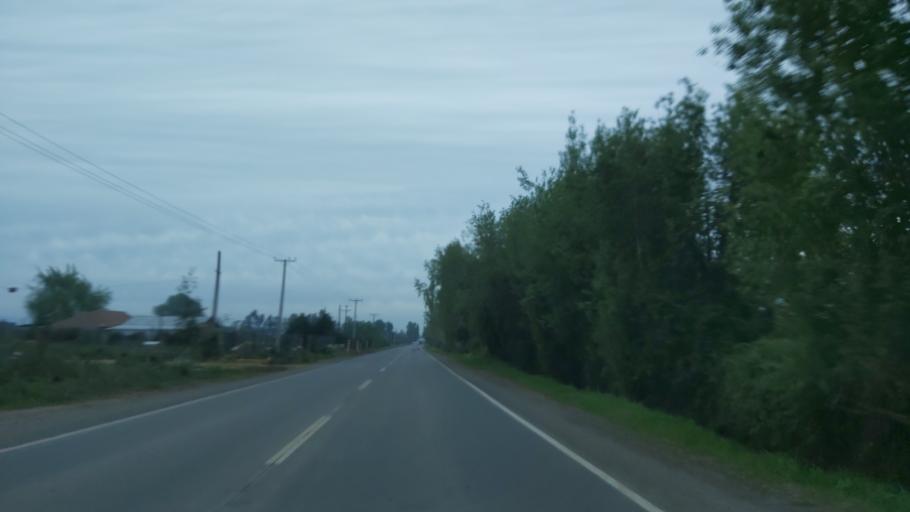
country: CL
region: Maule
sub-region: Provincia de Linares
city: Colbun
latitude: -35.7449
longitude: -71.4924
